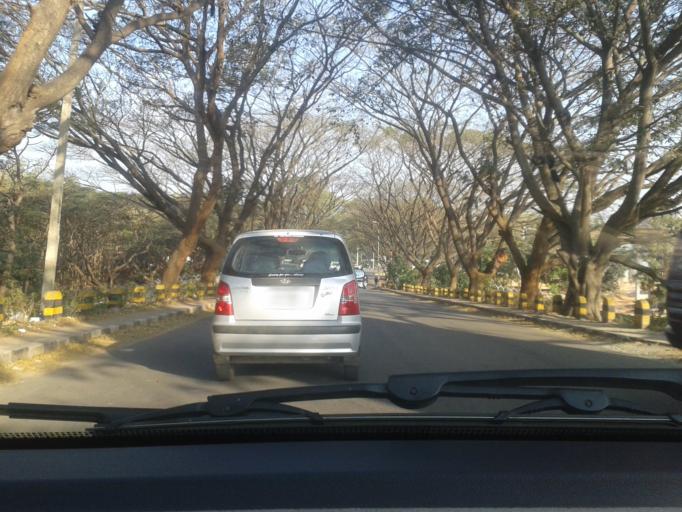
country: IN
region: Karnataka
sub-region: Bangalore Urban
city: Yelahanka
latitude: 13.0422
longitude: 77.5619
